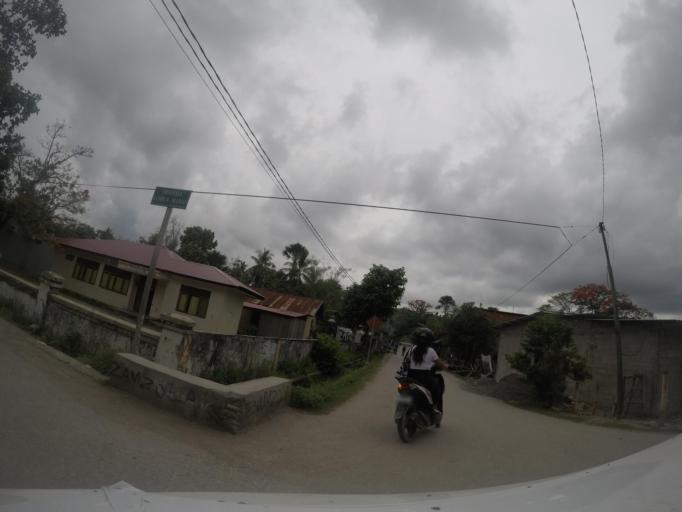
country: TL
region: Viqueque
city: Viqueque
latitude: -8.8577
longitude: 126.3633
